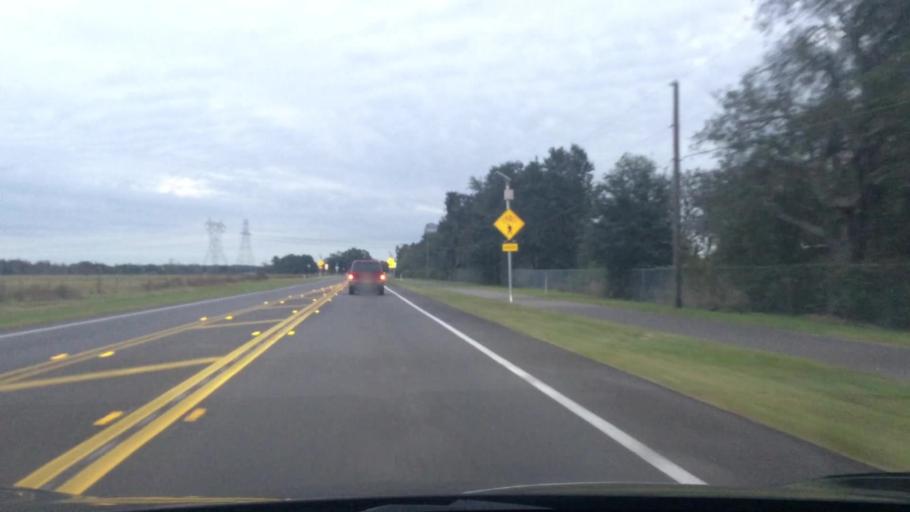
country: US
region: Florida
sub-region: Hillsborough County
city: Keystone
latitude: 28.1446
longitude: -82.6597
